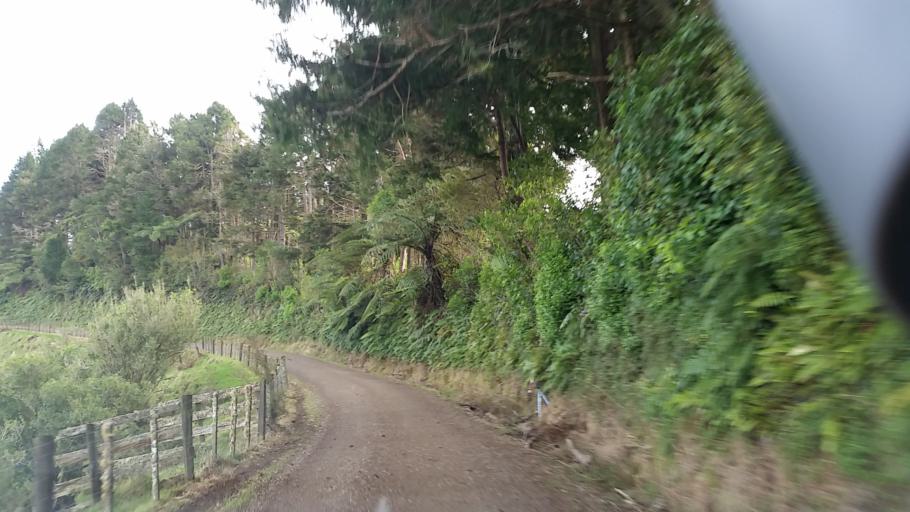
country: NZ
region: Taranaki
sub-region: New Plymouth District
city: Waitara
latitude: -39.0527
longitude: 174.3974
